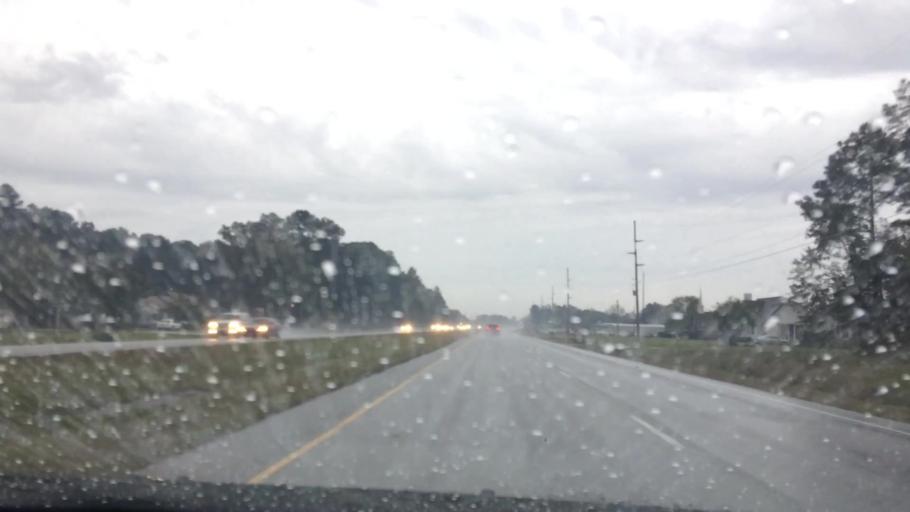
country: US
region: North Carolina
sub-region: Pitt County
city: Grifton
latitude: 35.4168
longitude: -77.4347
